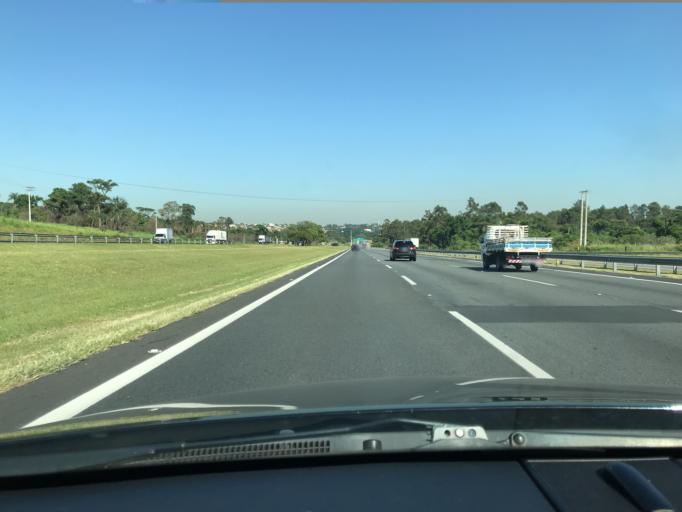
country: BR
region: Sao Paulo
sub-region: Valinhos
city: Valinhos
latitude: -23.0138
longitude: -47.0853
